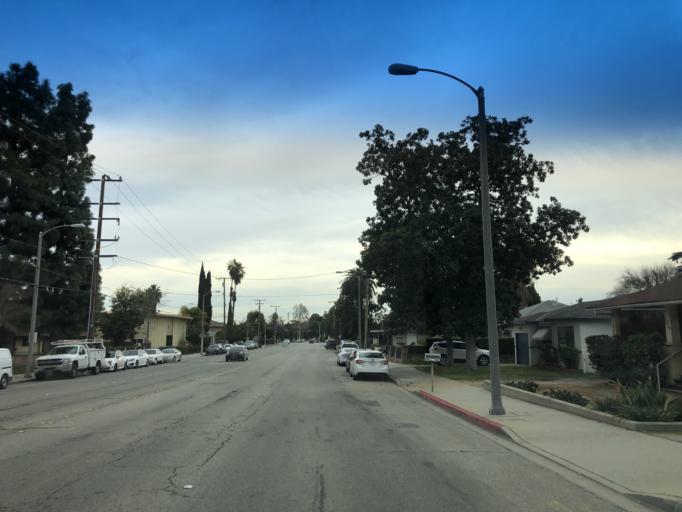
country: US
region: California
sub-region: Los Angeles County
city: Monrovia
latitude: 34.1345
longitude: -118.0096
